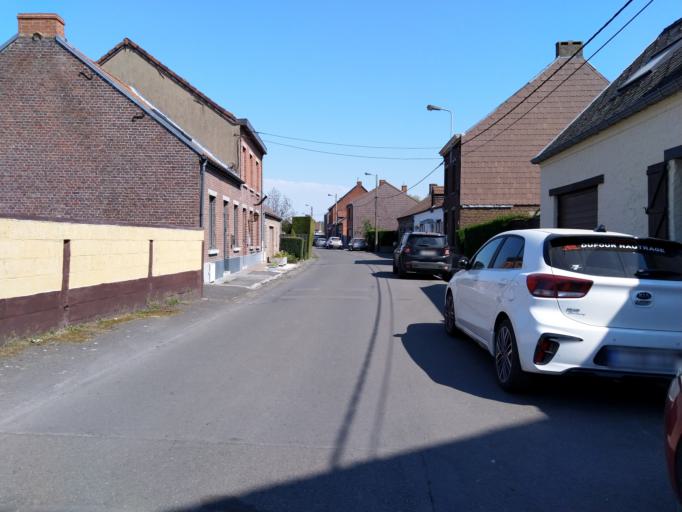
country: BE
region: Wallonia
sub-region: Province du Hainaut
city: Jurbise
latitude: 50.4819
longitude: 3.9114
